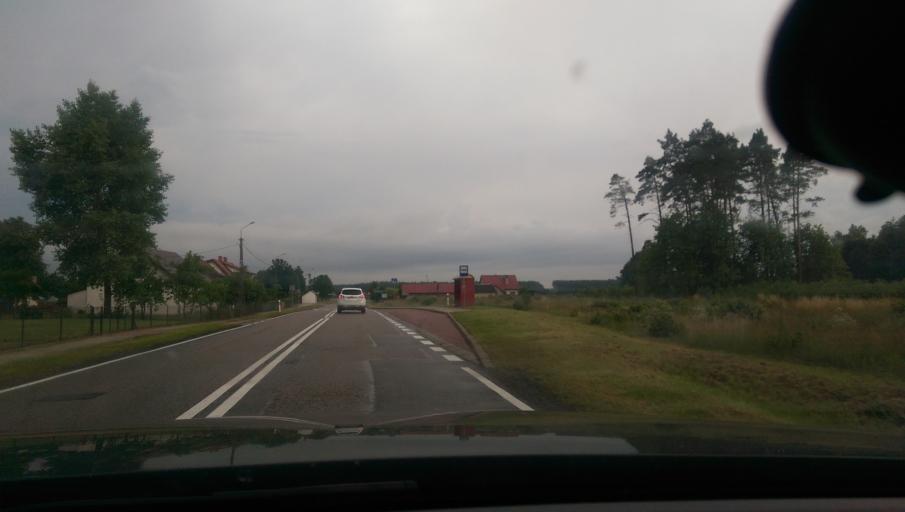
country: PL
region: Warmian-Masurian Voivodeship
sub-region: Powiat szczycienski
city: Szczytno
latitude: 53.5052
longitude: 20.9678
